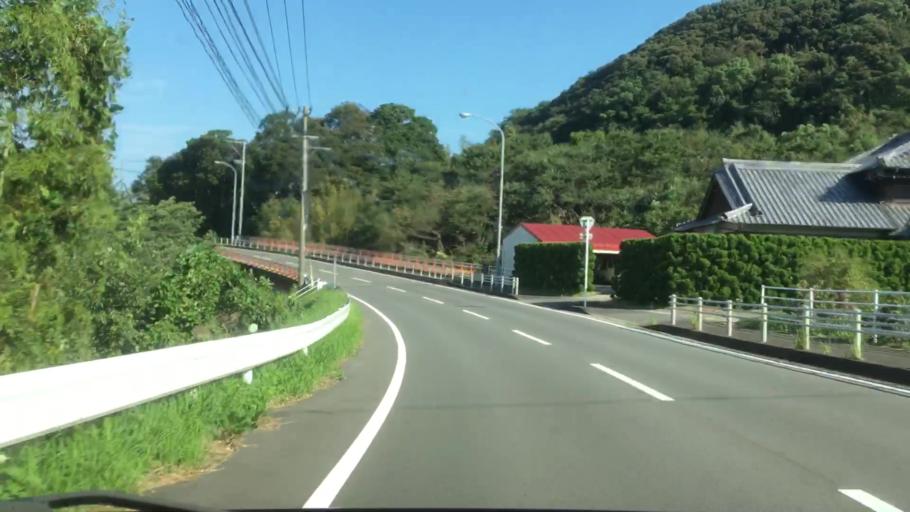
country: JP
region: Nagasaki
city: Sasebo
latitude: 33.0079
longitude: 129.6571
